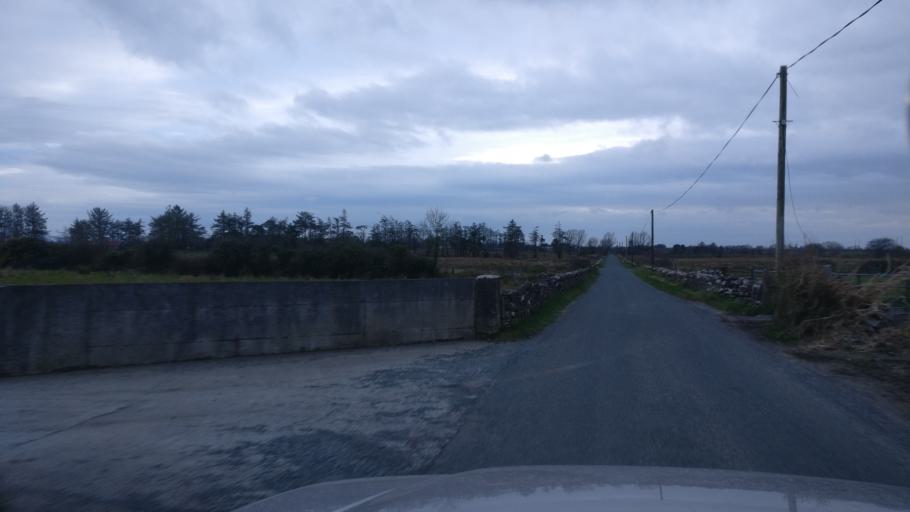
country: IE
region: Connaught
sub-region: County Galway
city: Loughrea
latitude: 53.2675
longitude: -8.4865
